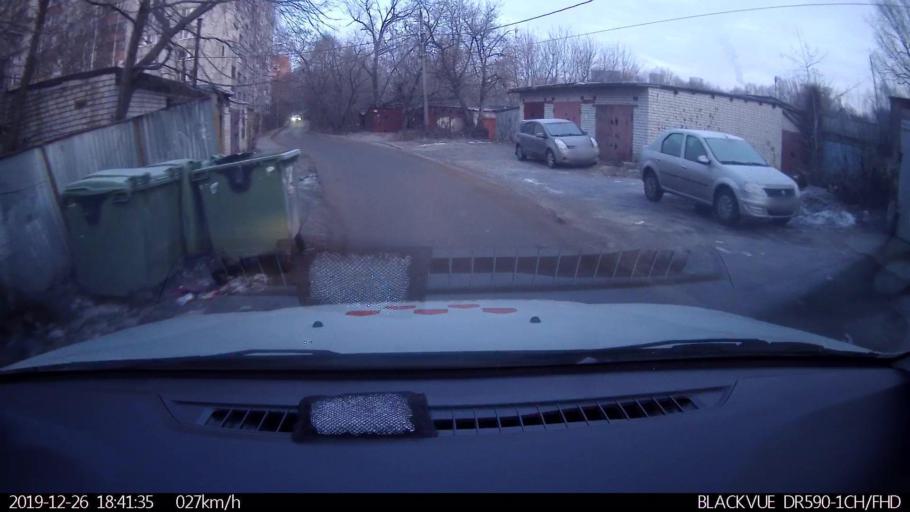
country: RU
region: Nizjnij Novgorod
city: Nizhniy Novgorod
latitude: 56.3163
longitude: 44.0346
